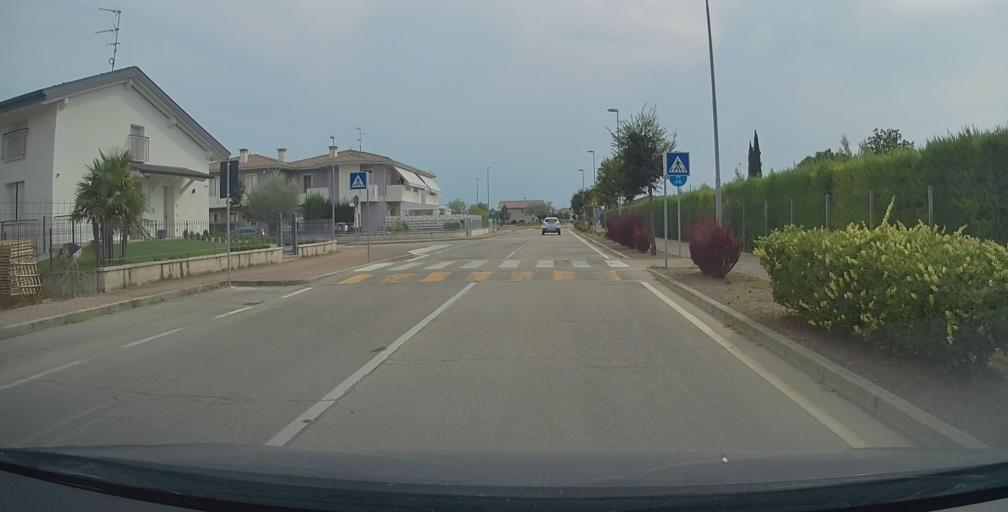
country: IT
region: Veneto
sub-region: Provincia di Verona
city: Mozzecane
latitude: 45.3125
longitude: 10.8118
